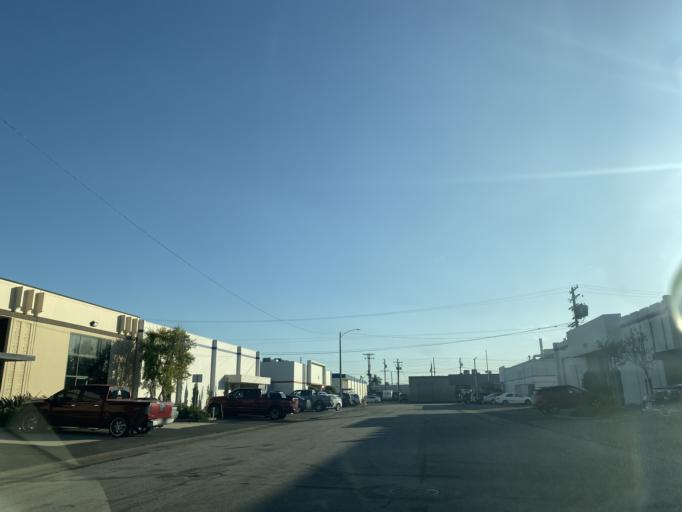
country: US
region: California
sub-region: Orange County
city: Fullerton
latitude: 33.8621
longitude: -117.9163
